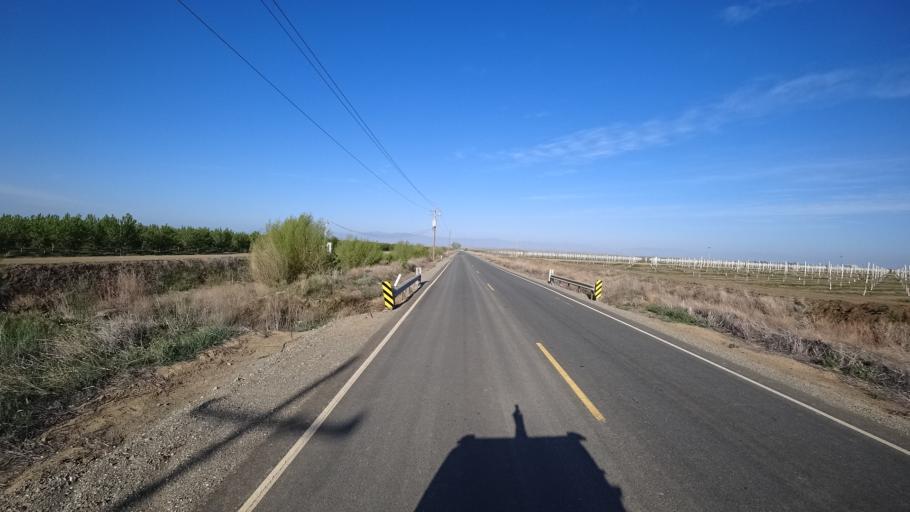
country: US
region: California
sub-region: Glenn County
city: Willows
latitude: 39.5824
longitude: -122.2389
